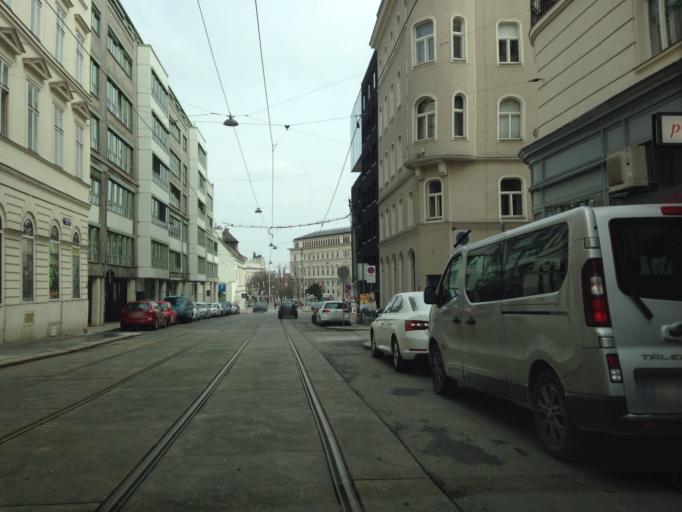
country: AT
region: Vienna
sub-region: Wien Stadt
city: Vienna
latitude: 48.2066
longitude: 16.3535
